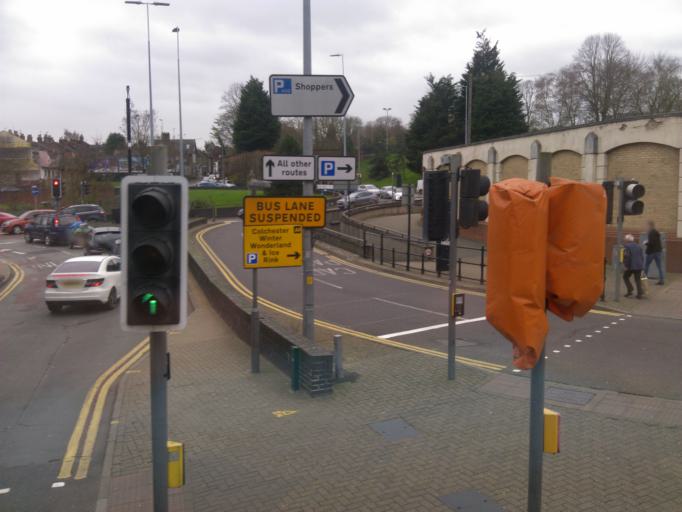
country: GB
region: England
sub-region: Essex
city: Colchester
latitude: 51.8869
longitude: 0.9034
